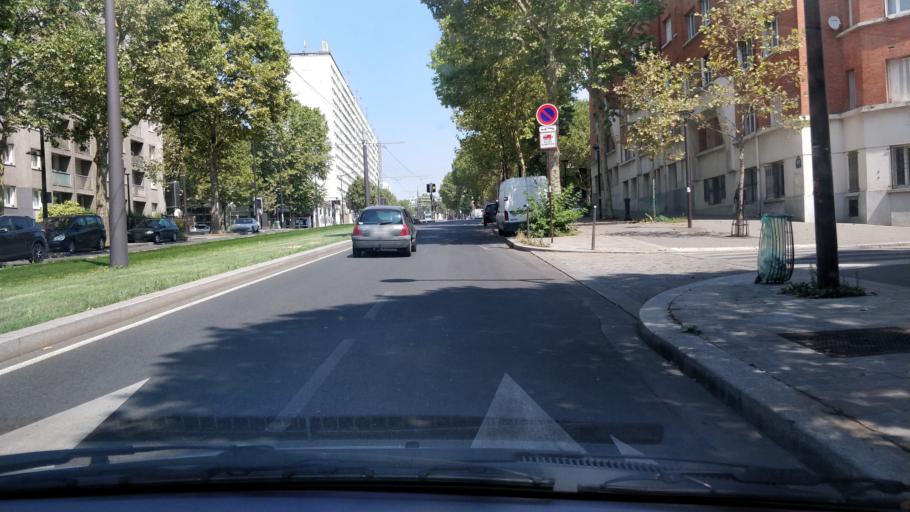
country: FR
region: Ile-de-France
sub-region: Departement de Seine-Saint-Denis
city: Bagnolet
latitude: 48.8695
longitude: 2.4090
